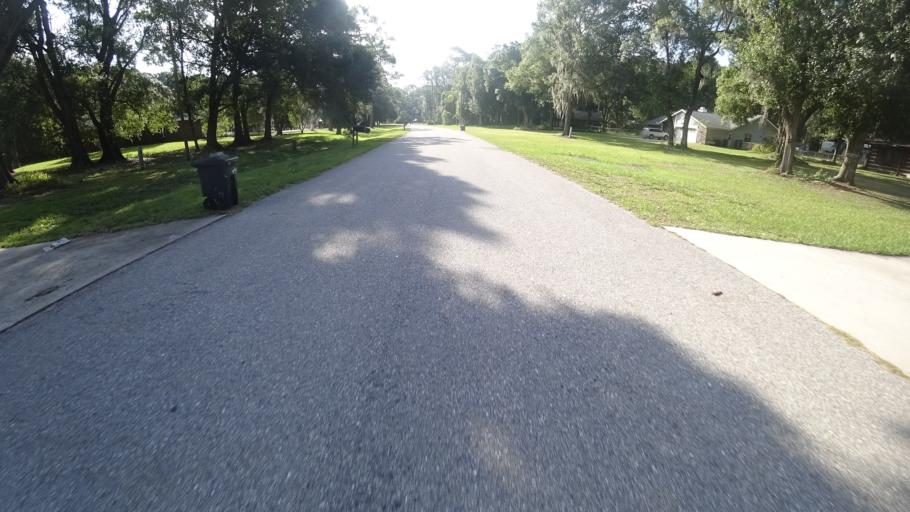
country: US
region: Florida
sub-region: Sarasota County
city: The Meadows
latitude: 27.4382
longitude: -82.4373
